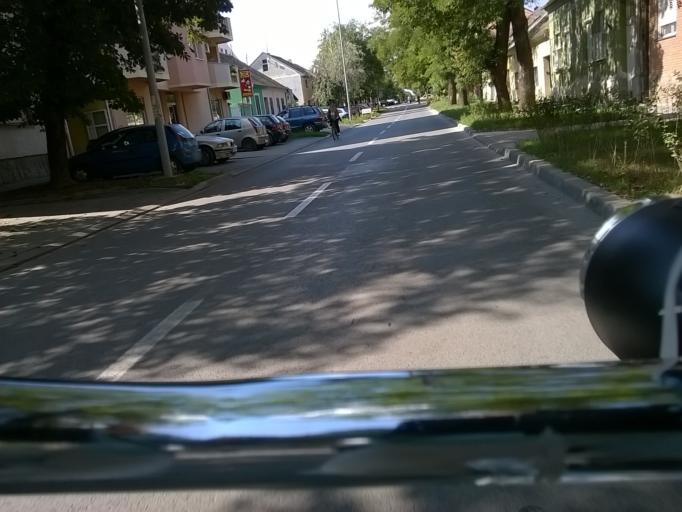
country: RS
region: Autonomna Pokrajina Vojvodina
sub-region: Juznobanatski Okrug
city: Pancevo
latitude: 44.8750
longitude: 20.6407
